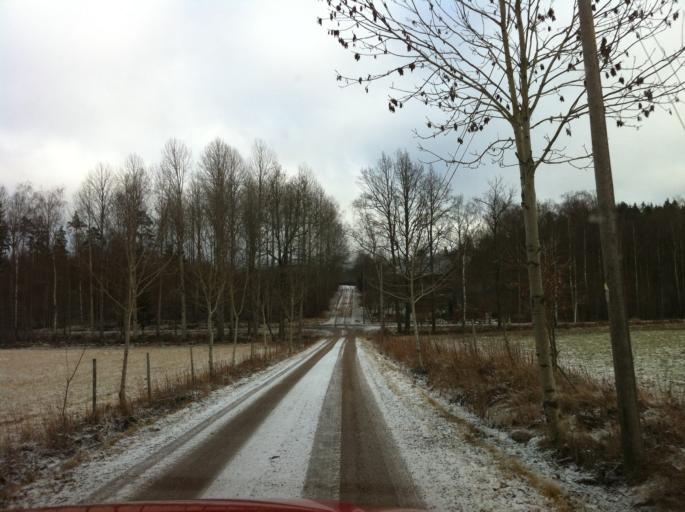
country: SE
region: Joenkoeping
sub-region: Eksjo Kommun
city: Mariannelund
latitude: 57.6185
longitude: 15.7090
